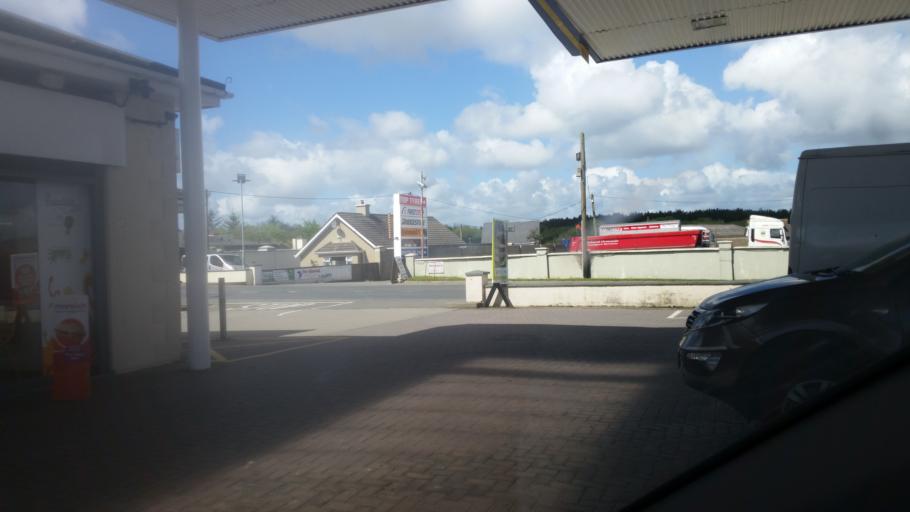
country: IE
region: Leinster
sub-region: Loch Garman
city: Castlebridge
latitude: 52.3665
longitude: -6.4489
